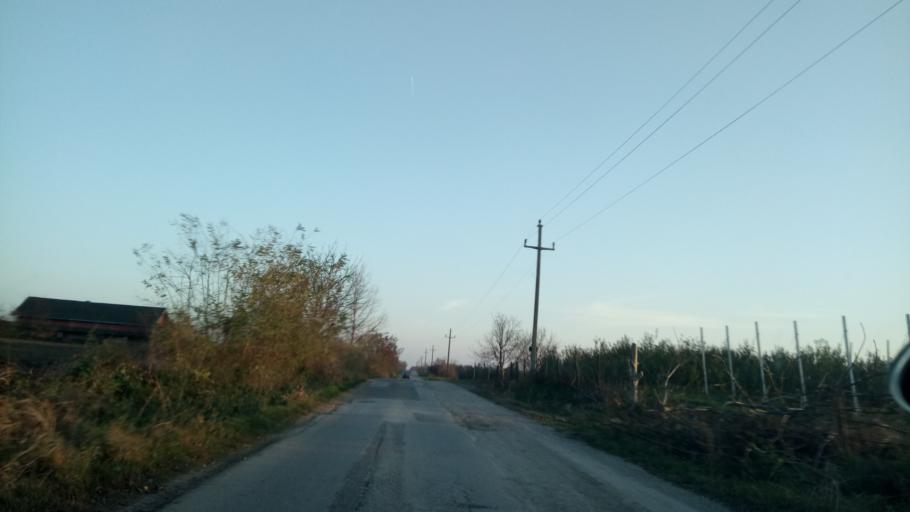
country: RS
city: Novi Slankamen
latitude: 45.1272
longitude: 20.2595
